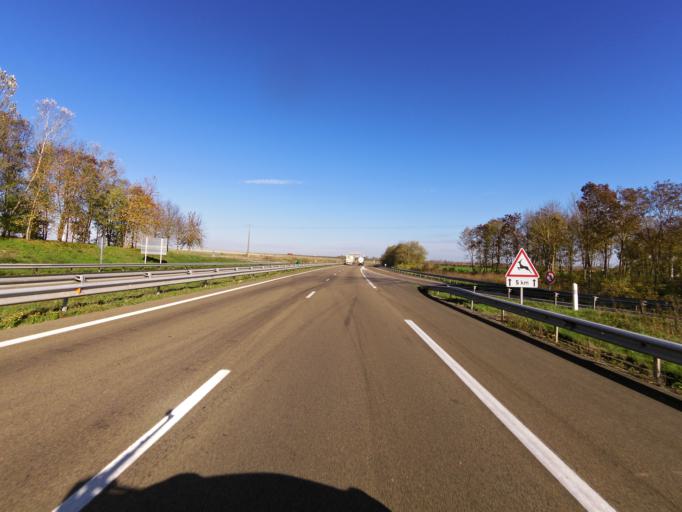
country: FR
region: Champagne-Ardenne
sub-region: Departement de la Marne
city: Fagnieres
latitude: 48.9714
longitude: 4.2841
